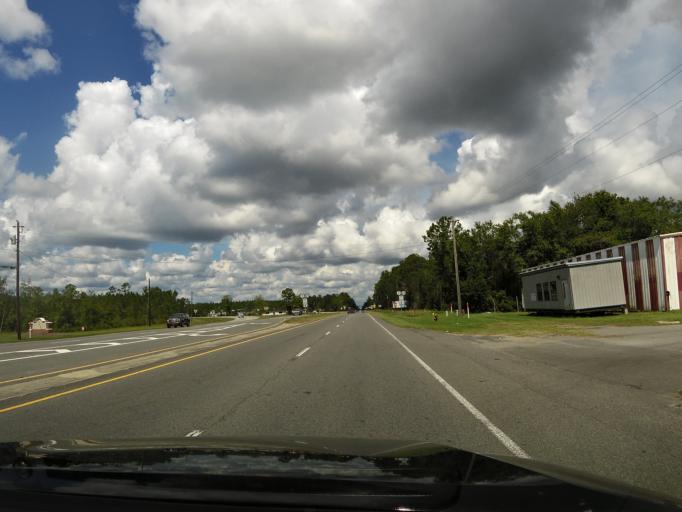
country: US
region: Georgia
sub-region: Charlton County
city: Folkston
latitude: 30.8606
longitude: -82.0110
